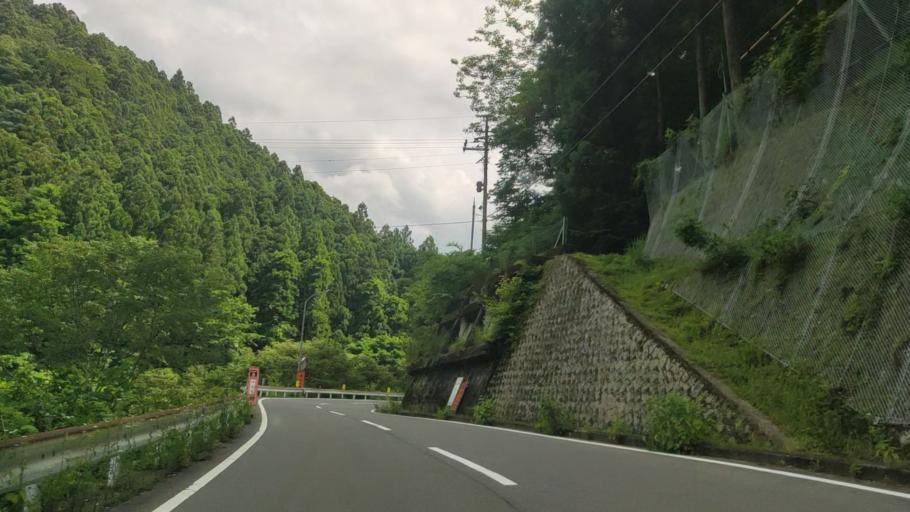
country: JP
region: Gunma
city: Tomioka
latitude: 36.1642
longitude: 138.7297
